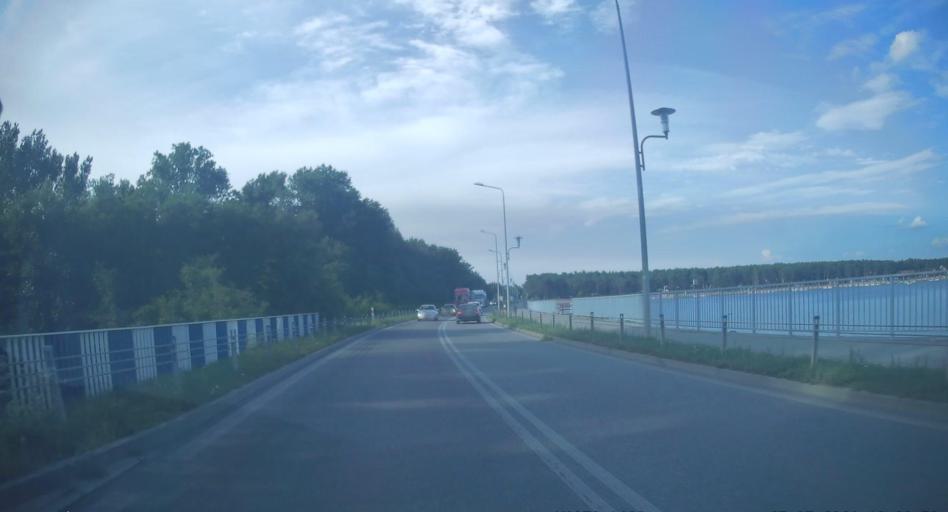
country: PL
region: Swietokrzyskie
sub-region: Powiat konecki
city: Smykow
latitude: 51.1145
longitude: 20.3496
